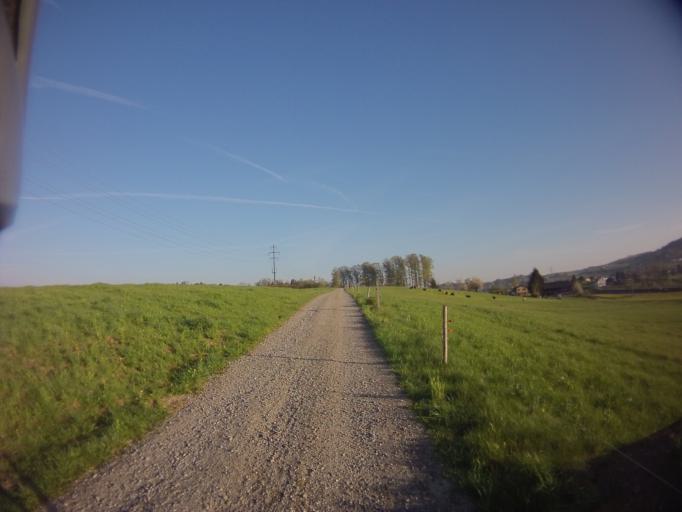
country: CH
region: Zurich
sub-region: Bezirk Affoltern
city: Mettmenstetten
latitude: 47.2360
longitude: 8.4549
